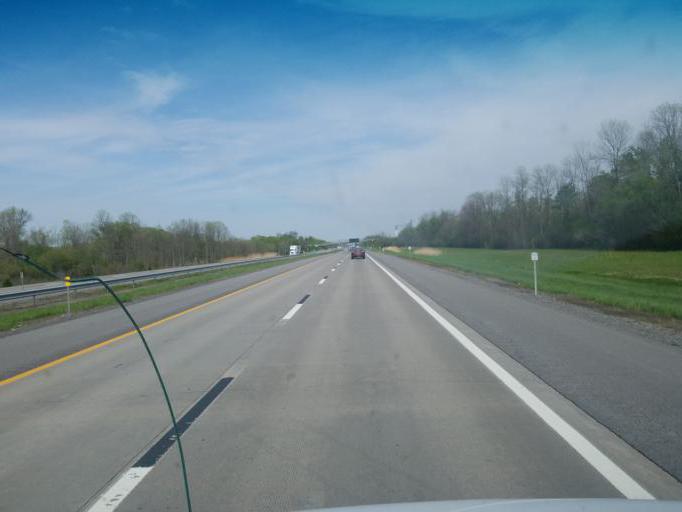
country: US
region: New York
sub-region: Onondaga County
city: Jordan
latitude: 43.0759
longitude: -76.4888
